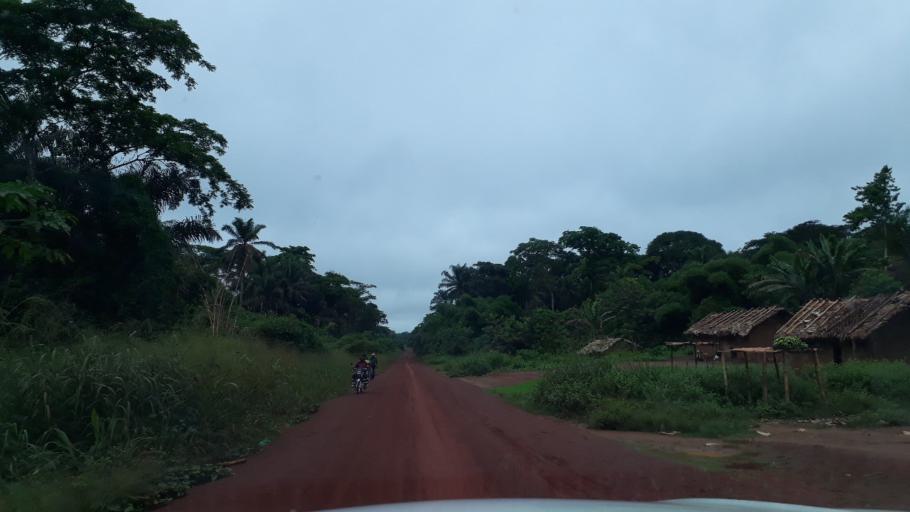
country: CD
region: Eastern Province
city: Wamba
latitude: 1.3687
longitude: 27.5966
